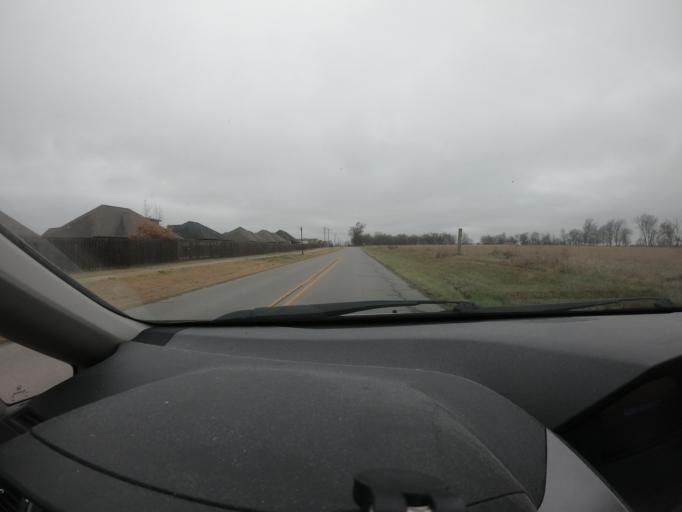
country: US
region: Arkansas
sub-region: Benton County
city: Bentonville
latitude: 36.3486
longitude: -94.2403
